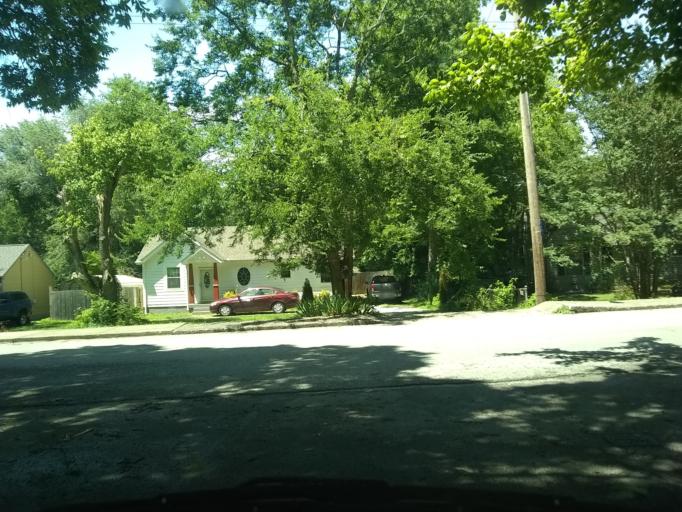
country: US
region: Tennessee
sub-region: Davidson County
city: Oak Hill
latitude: 36.1271
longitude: -86.7039
